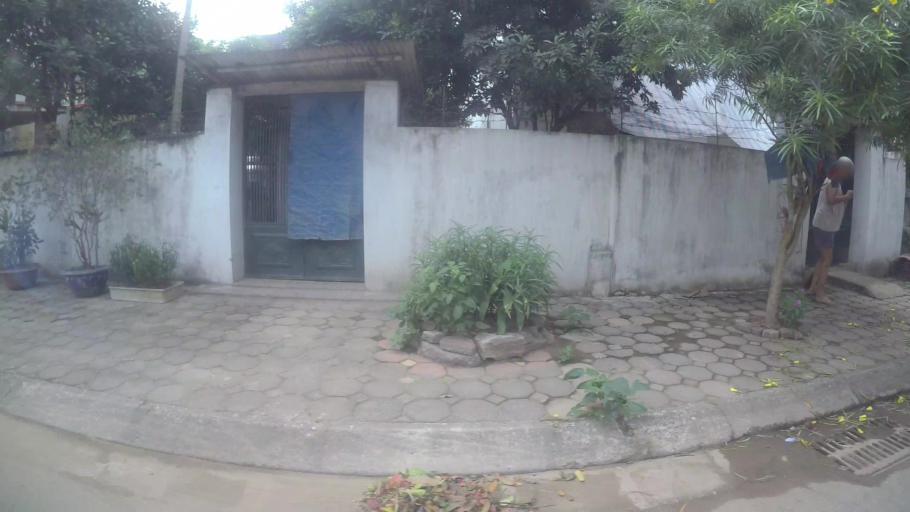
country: VN
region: Ha Noi
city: Tay Ho
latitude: 21.0875
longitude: 105.7956
